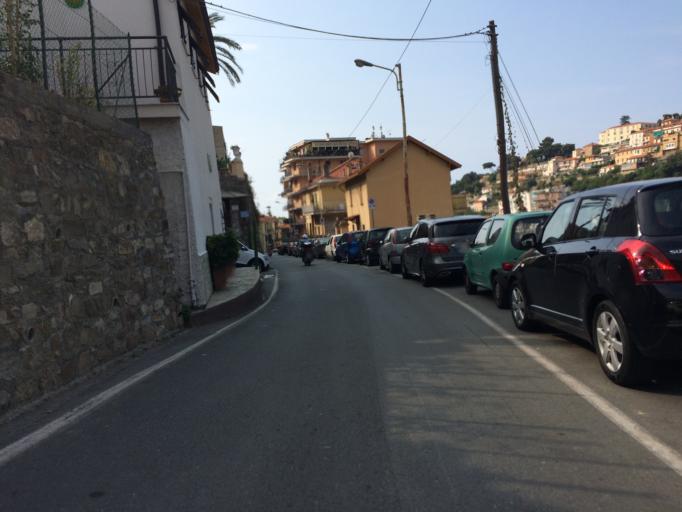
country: IT
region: Liguria
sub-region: Provincia di Imperia
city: San Remo
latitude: 43.8250
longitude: 7.7750
